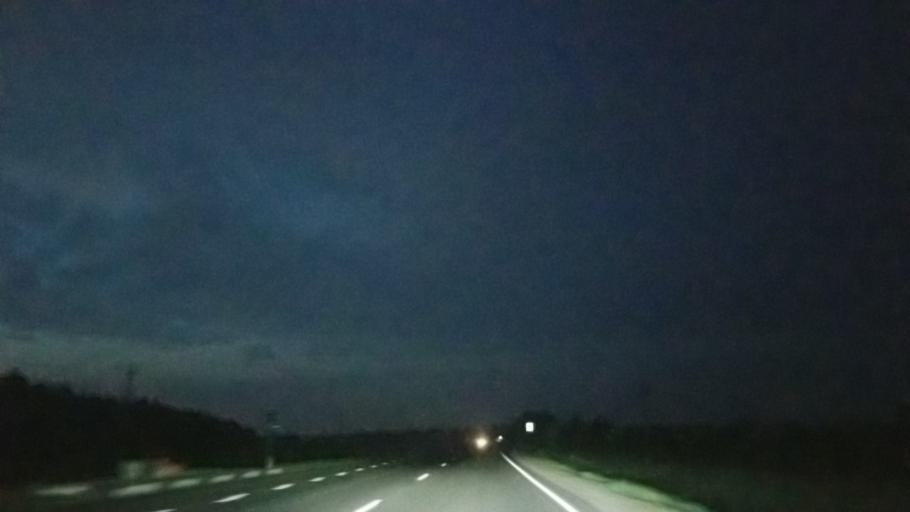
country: BY
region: Brest
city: Brest
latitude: 52.0000
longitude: 23.7138
